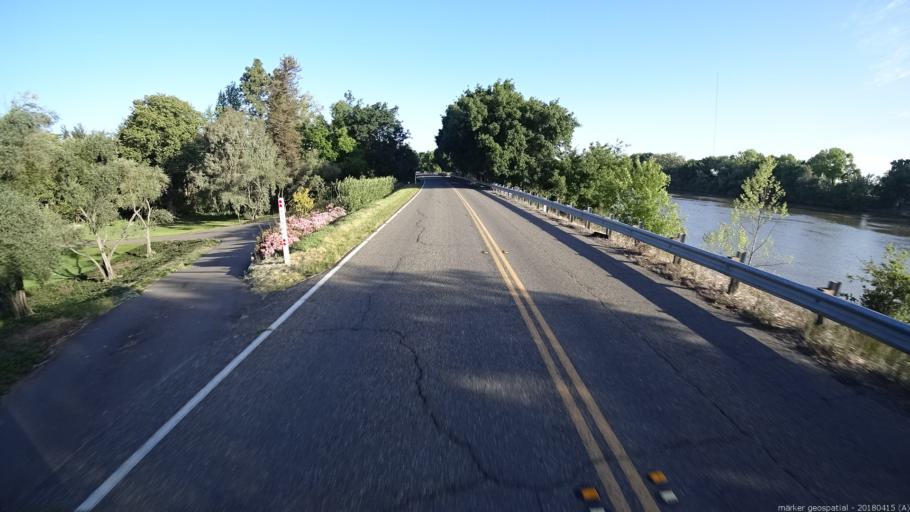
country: US
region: California
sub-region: Sacramento County
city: Walnut Grove
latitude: 38.2521
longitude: -121.5128
